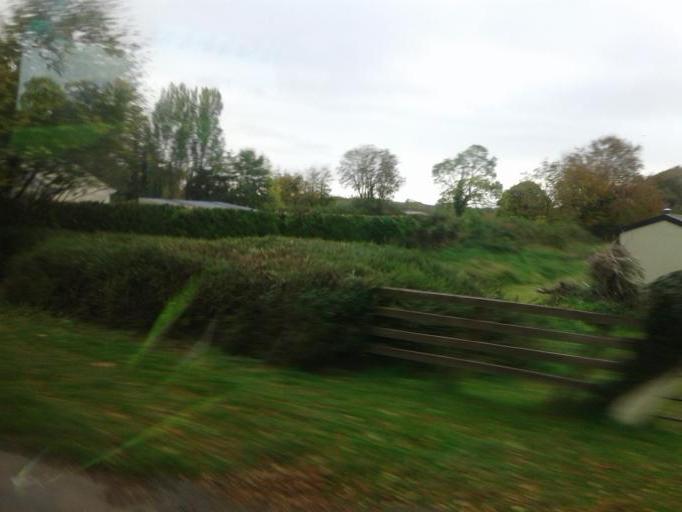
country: IE
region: Munster
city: Nenagh Bridge
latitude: 52.9496
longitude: -8.0347
